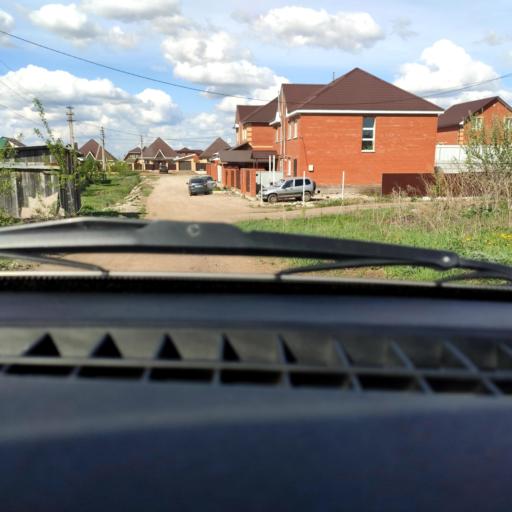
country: RU
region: Bashkortostan
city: Avdon
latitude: 54.6982
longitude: 55.7940
